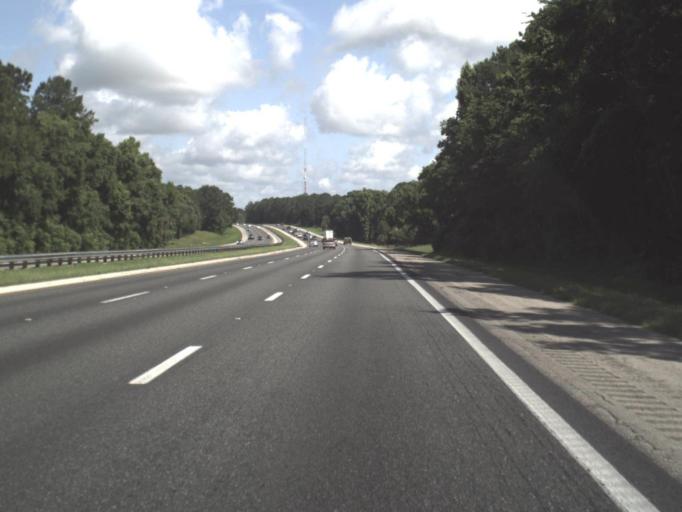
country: US
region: Florida
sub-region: Alachua County
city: Gainesville
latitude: 29.5262
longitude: -82.3125
